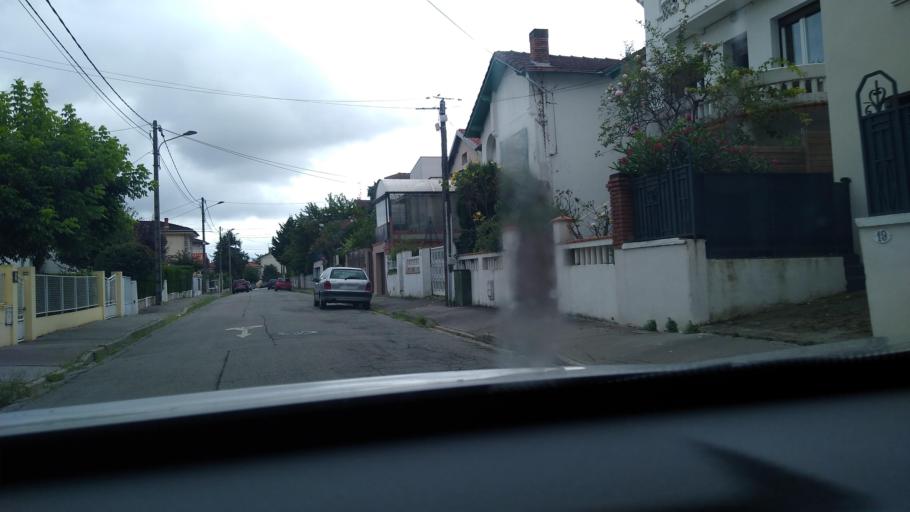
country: FR
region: Midi-Pyrenees
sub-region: Departement de la Haute-Garonne
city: Toulouse
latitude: 43.6255
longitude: 1.4632
